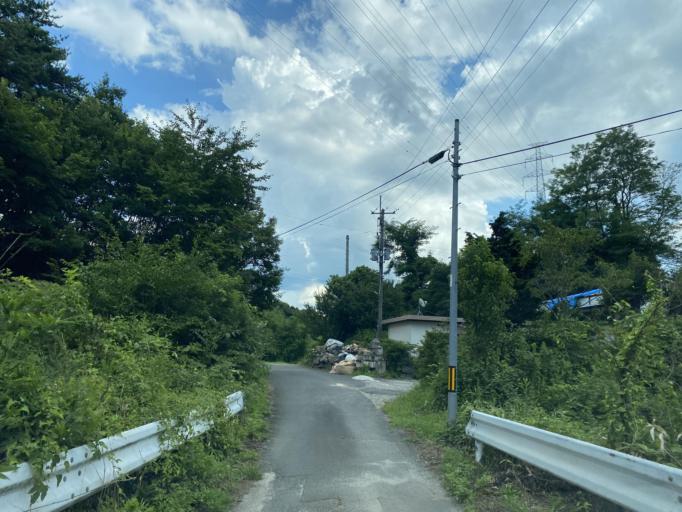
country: JP
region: Fukushima
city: Koriyama
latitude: 37.3772
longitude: 140.4210
